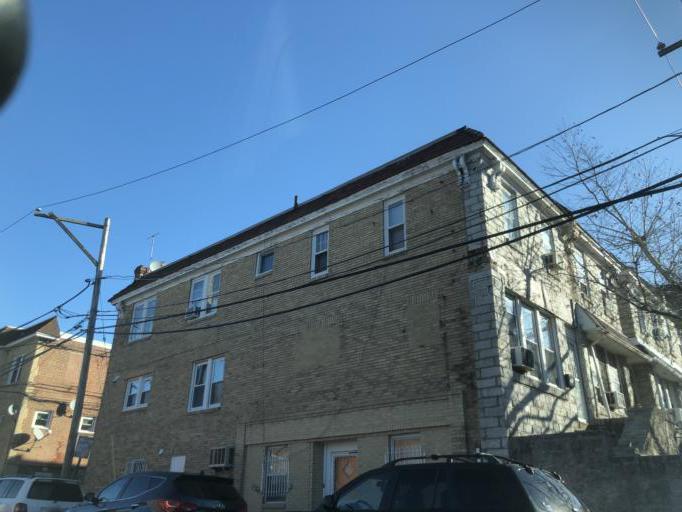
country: US
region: Pennsylvania
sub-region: Delaware County
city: East Lansdowne
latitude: 39.9557
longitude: -75.2677
